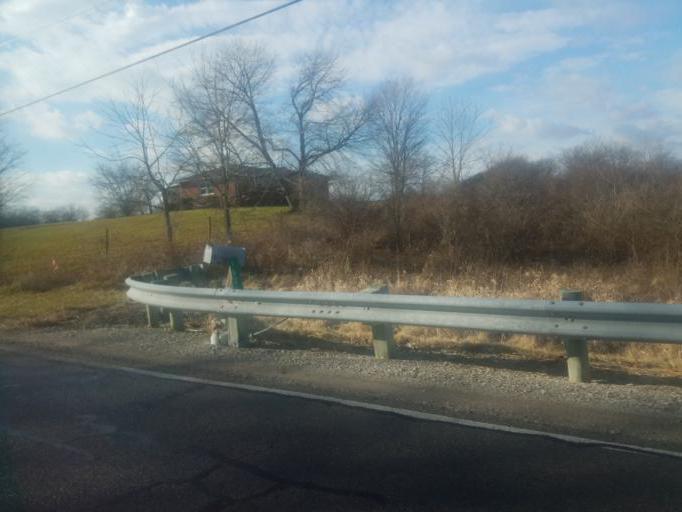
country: US
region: Ohio
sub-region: Marion County
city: Marion
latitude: 40.5586
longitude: -83.1598
